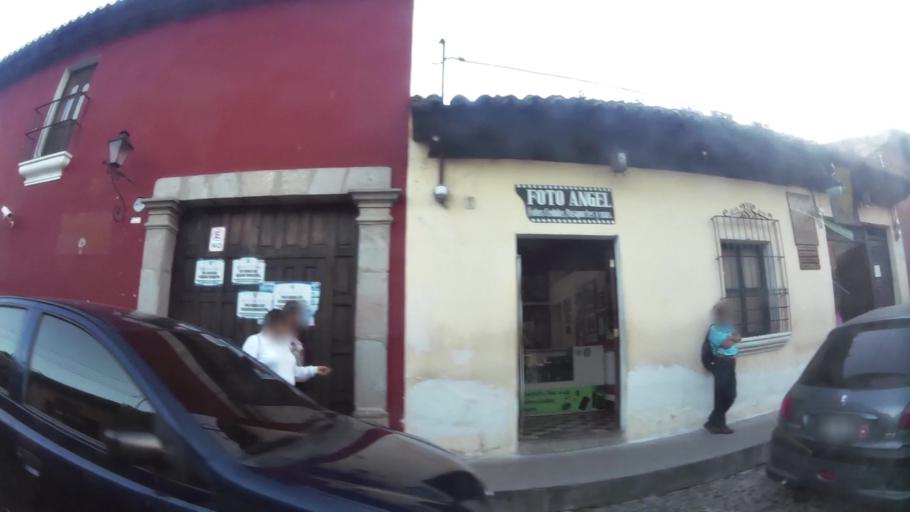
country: GT
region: Sacatepequez
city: Antigua Guatemala
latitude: 14.5562
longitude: -90.7372
